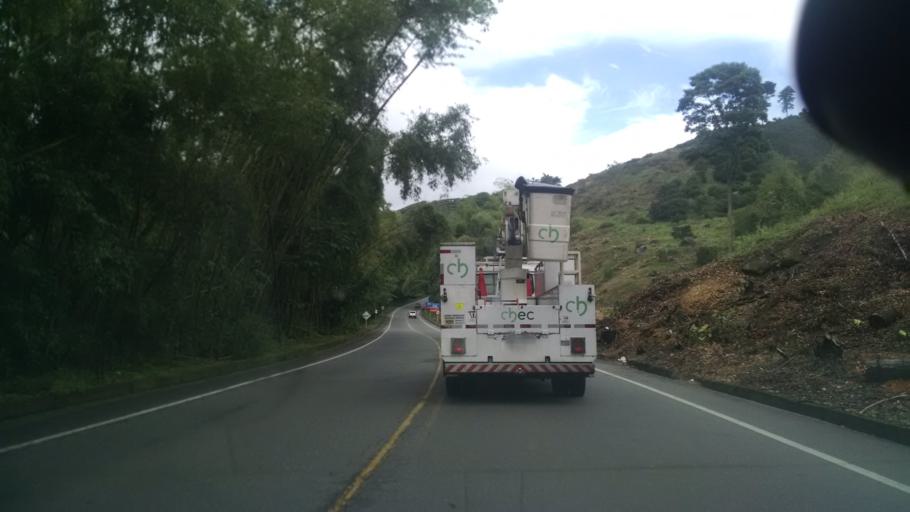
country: CO
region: Caldas
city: Palestina
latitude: 5.0619
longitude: -75.6114
